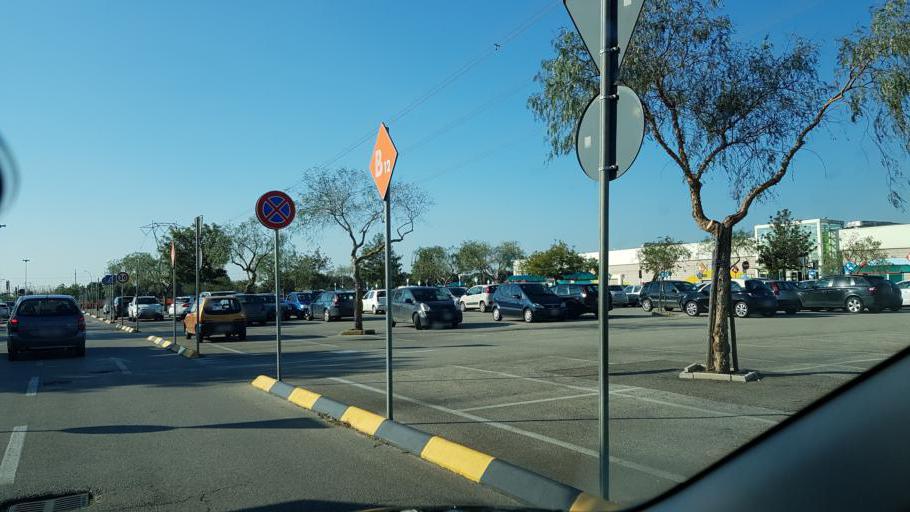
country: IT
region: Apulia
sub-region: Provincia di Brindisi
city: Mesagne
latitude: 40.5796
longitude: 17.8360
